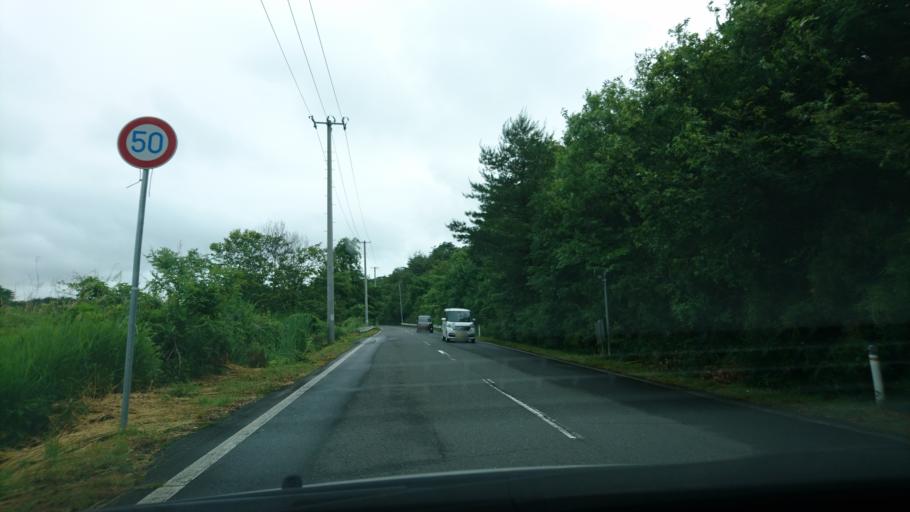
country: JP
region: Iwate
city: Ichinoseki
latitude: 38.8907
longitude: 141.1508
